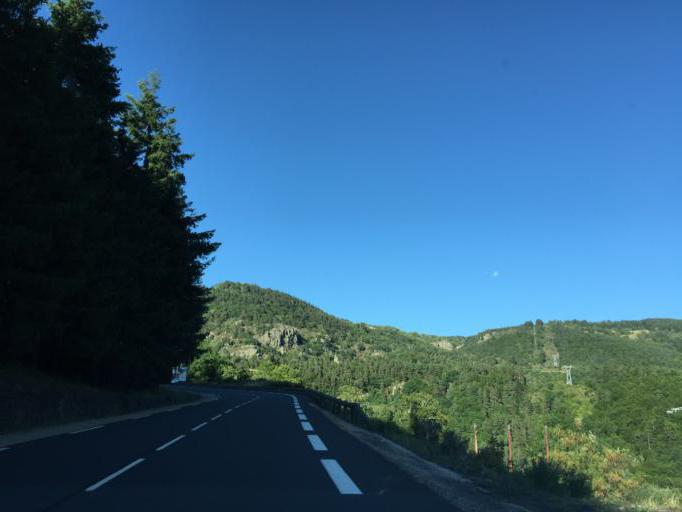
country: FR
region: Auvergne
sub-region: Departement de la Haute-Loire
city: Bains
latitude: 44.9783
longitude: 3.6755
